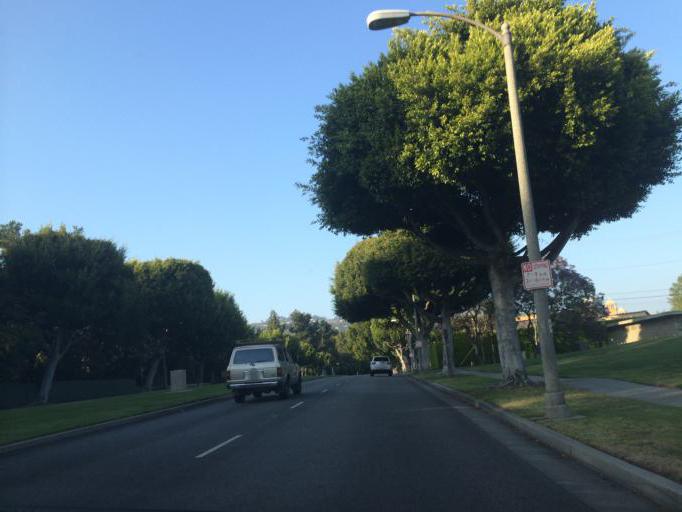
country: US
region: California
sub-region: Los Angeles County
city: Beverly Hills
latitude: 34.0835
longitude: -118.4096
